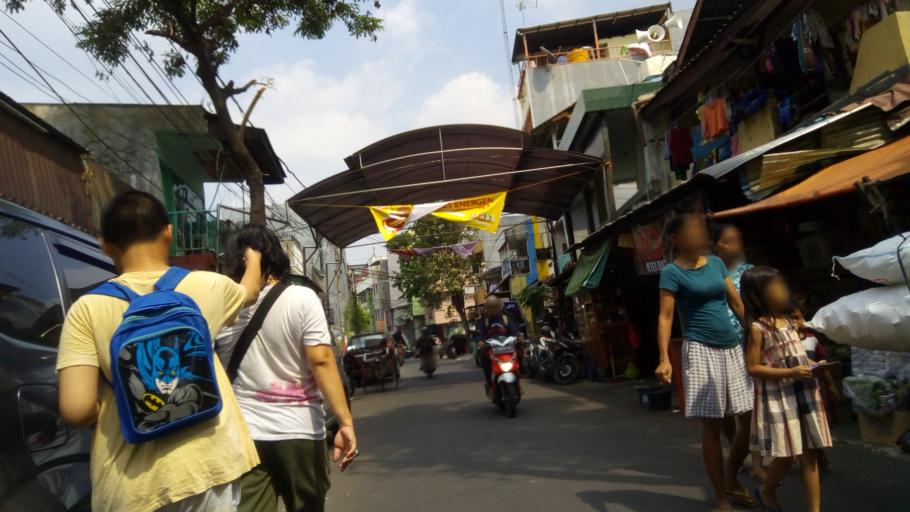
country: ID
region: Jakarta Raya
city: Jakarta
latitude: -6.1579
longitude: 106.8293
